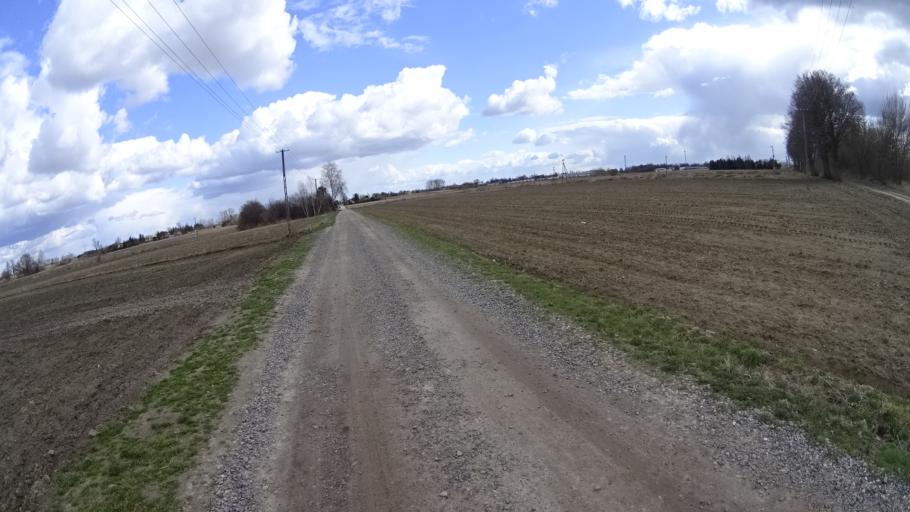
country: PL
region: Masovian Voivodeship
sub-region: Powiat warszawski zachodni
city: Jozefow
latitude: 52.2202
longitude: 20.6775
